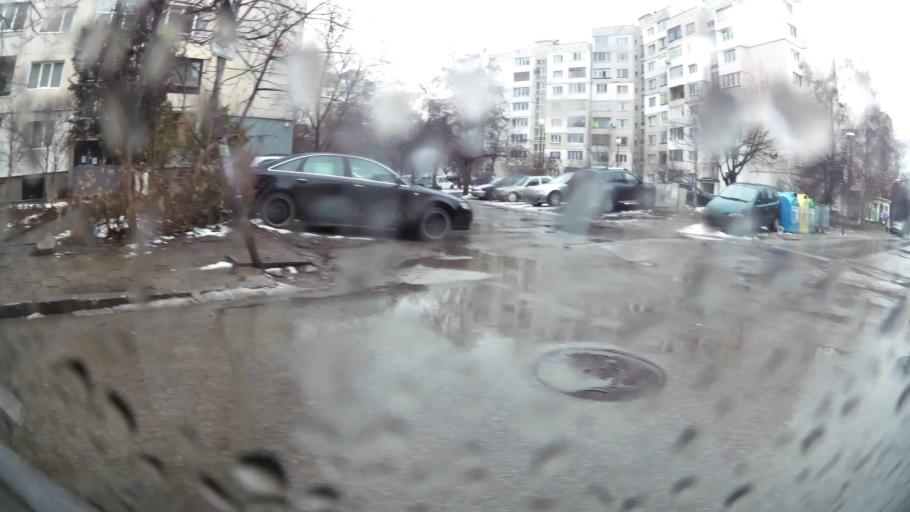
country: BG
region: Sofia-Capital
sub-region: Stolichna Obshtina
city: Sofia
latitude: 42.6680
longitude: 23.3023
